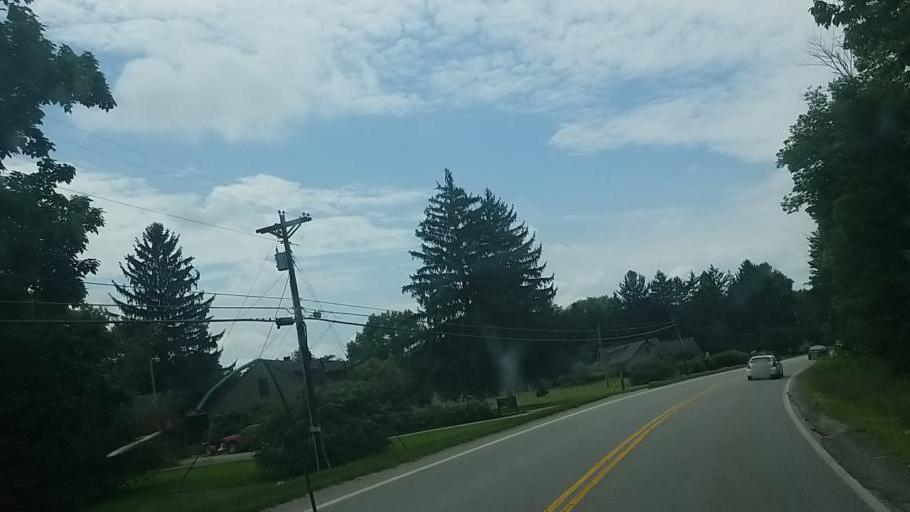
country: US
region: Ohio
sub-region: Franklin County
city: Obetz
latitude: 39.8308
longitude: -82.9813
